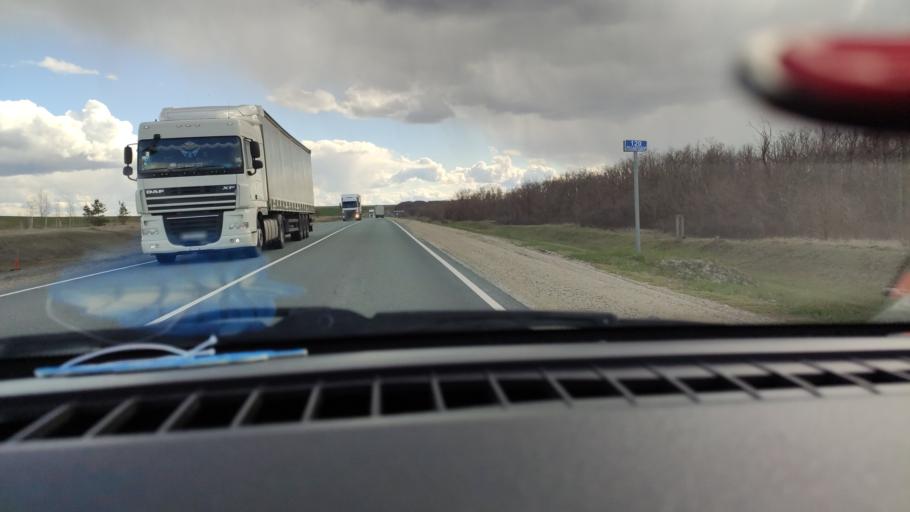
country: RU
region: Saratov
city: Alekseyevka
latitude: 52.2313
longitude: 47.9031
